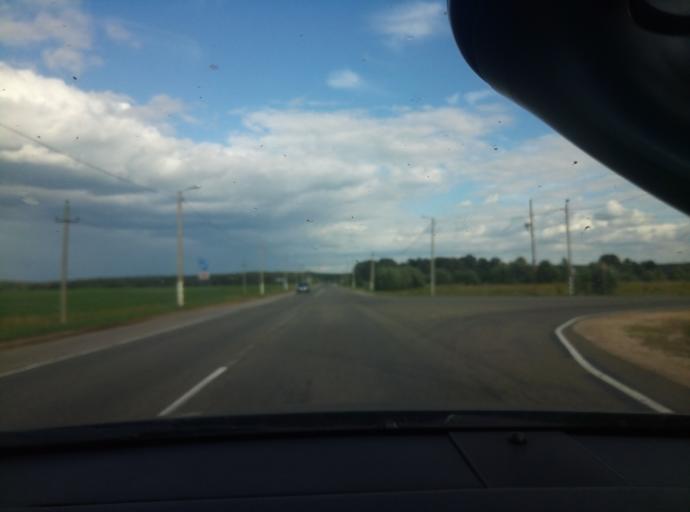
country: RU
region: Kaluga
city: Nikola-Lenivets
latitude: 54.5640
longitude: 35.4759
